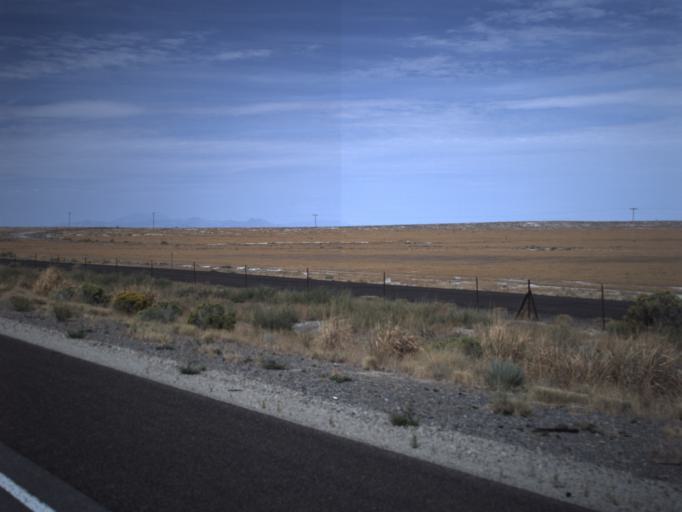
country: US
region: Utah
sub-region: Tooele County
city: Wendover
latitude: 40.7272
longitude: -113.2477
